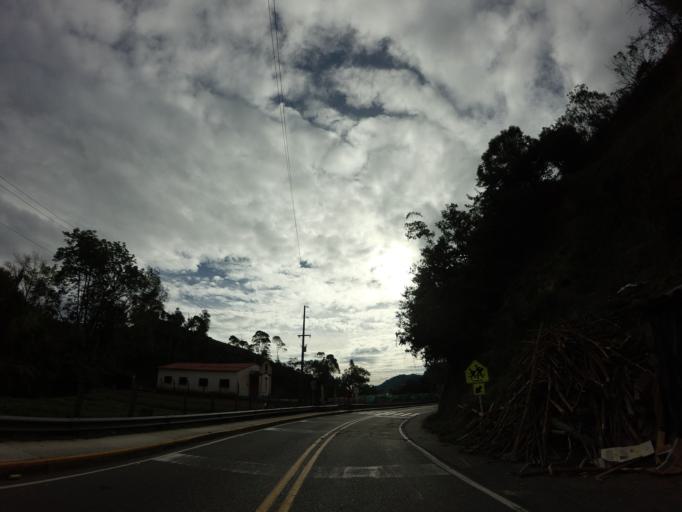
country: CO
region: Tolima
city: Herveo
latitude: 5.1341
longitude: -75.1930
